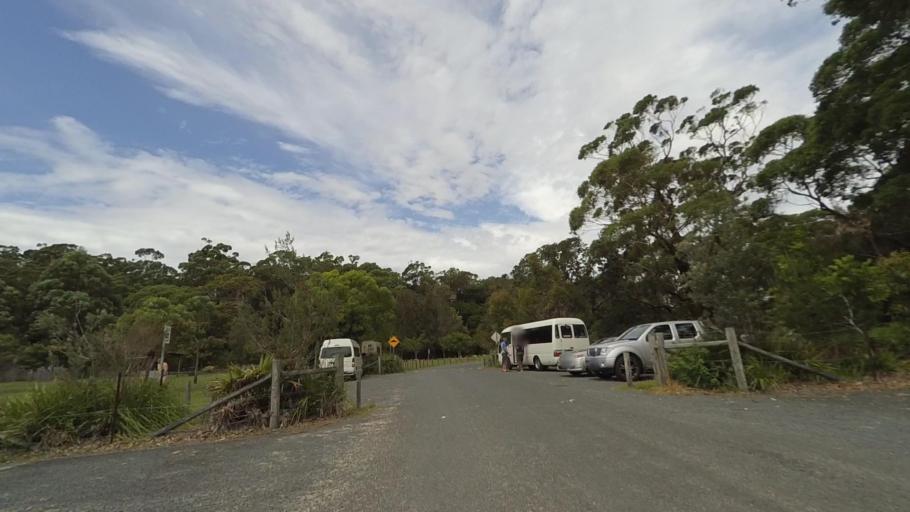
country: AU
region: New South Wales
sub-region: Sutherland Shire
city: Bundeena
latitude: -34.0829
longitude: 151.1412
